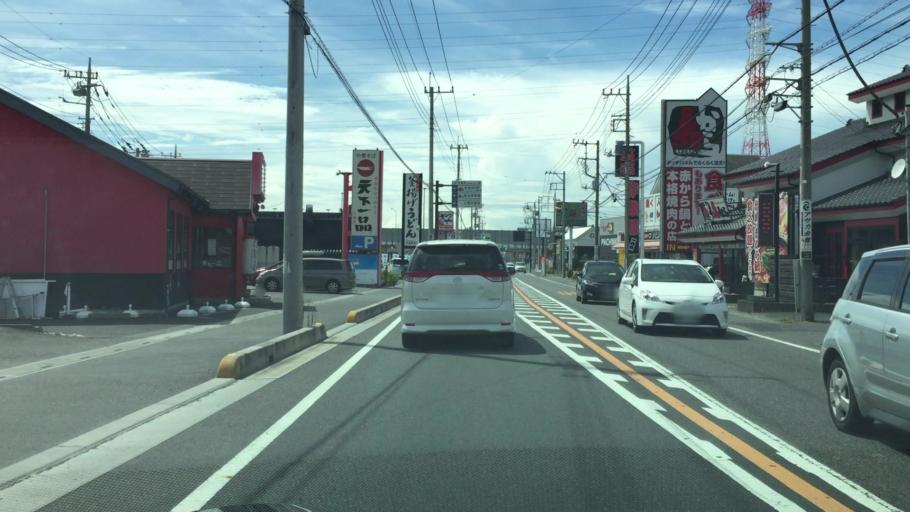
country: JP
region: Chiba
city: Nagareyama
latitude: 35.8468
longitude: 139.8766
